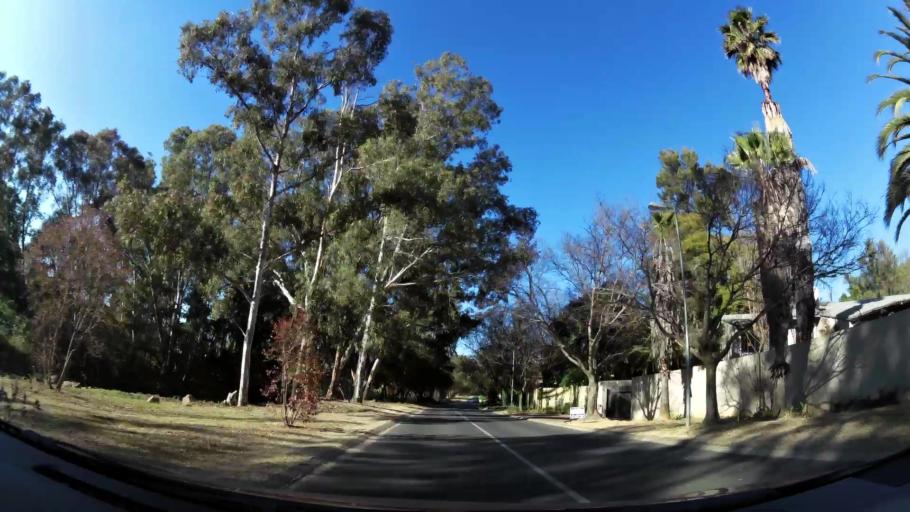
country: ZA
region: Gauteng
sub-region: City of Johannesburg Metropolitan Municipality
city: Diepsloot
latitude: -26.0476
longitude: 27.9872
